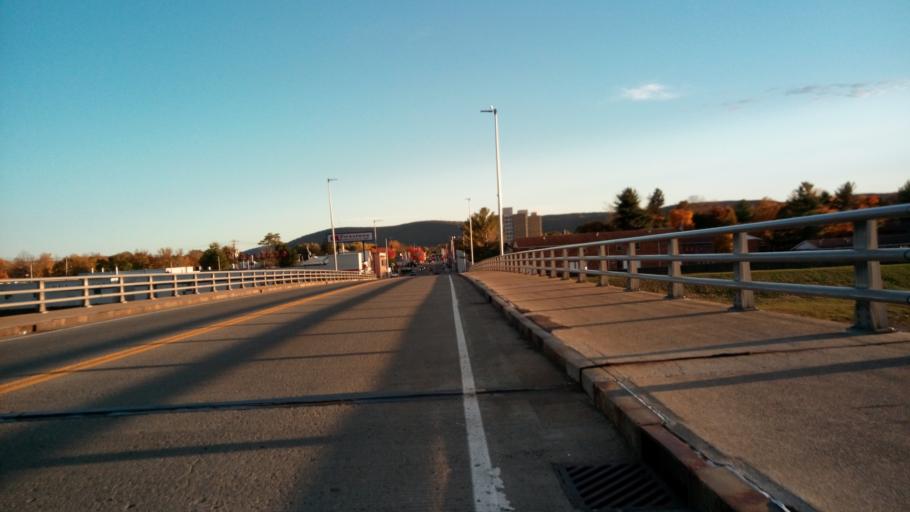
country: US
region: New York
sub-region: Chemung County
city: Elmira
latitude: 42.0862
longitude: -76.8065
